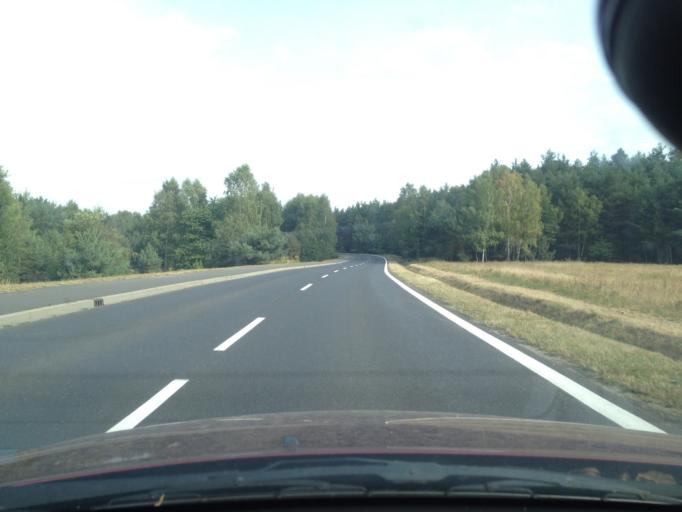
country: PL
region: Lubusz
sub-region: Powiat zaganski
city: Szprotawa
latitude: 51.4382
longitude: 15.6008
